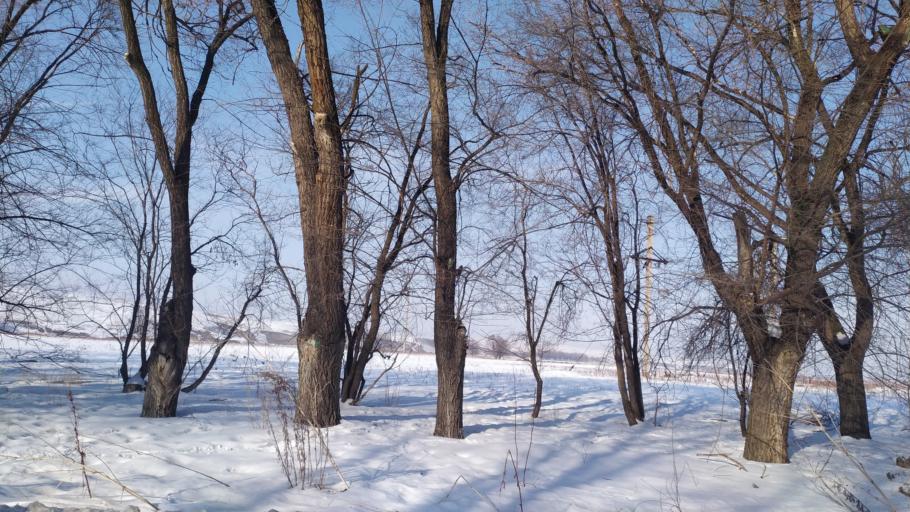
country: KZ
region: Almaty Oblysy
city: Burunday
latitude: 43.2343
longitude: 76.4077
